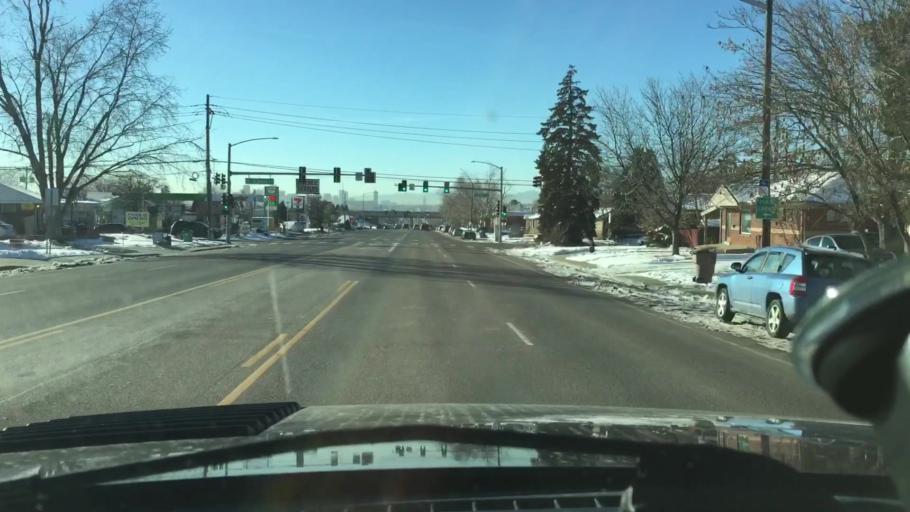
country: US
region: Colorado
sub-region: Adams County
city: Sherrelwood
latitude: 39.8353
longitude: -105.0062
